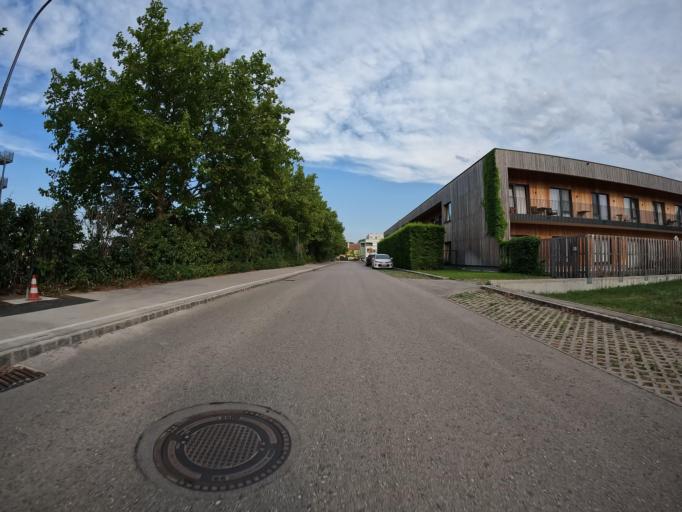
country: AT
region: Lower Austria
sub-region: Politischer Bezirk Baden
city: Traiskirchen
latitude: 48.0196
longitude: 16.2994
